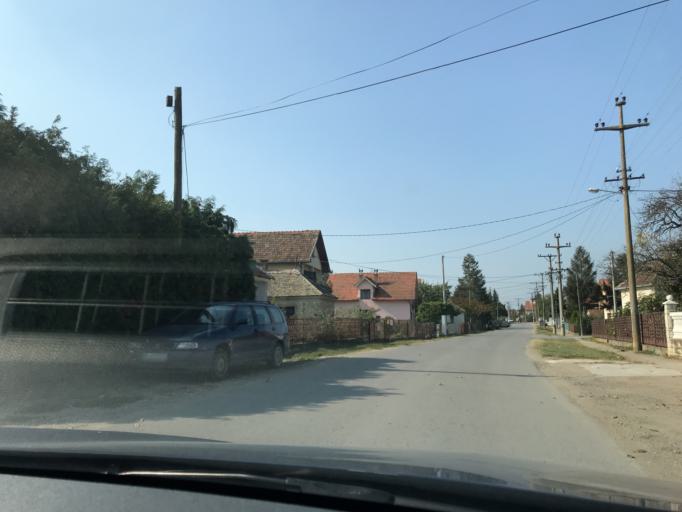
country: RS
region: Central Serbia
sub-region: Belgrade
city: Obrenovac
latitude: 44.6819
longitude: 20.2158
